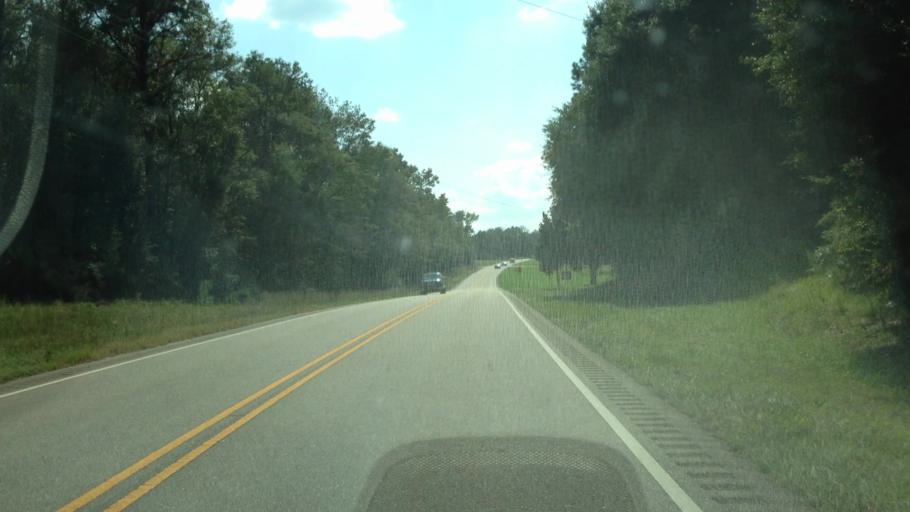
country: US
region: Alabama
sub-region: Covington County
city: Florala
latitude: 31.0535
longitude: -86.5794
